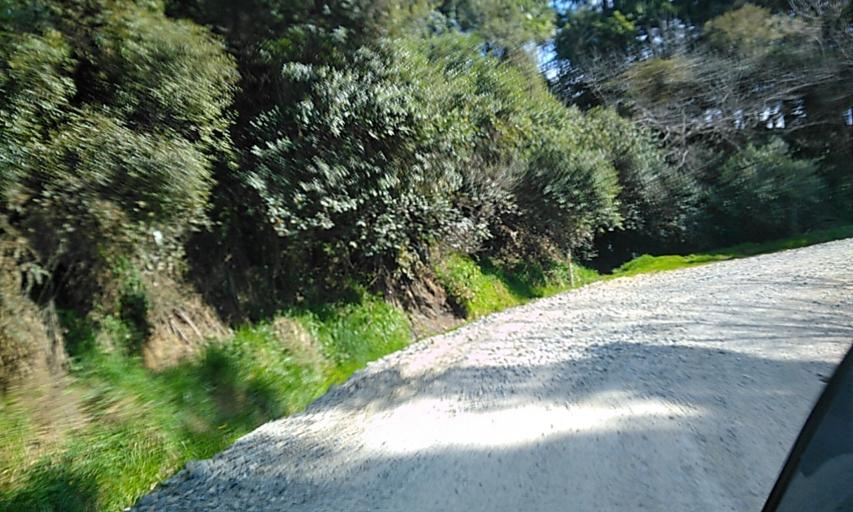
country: NZ
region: Gisborne
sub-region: Gisborne District
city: Gisborne
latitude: -38.2122
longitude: 178.0651
